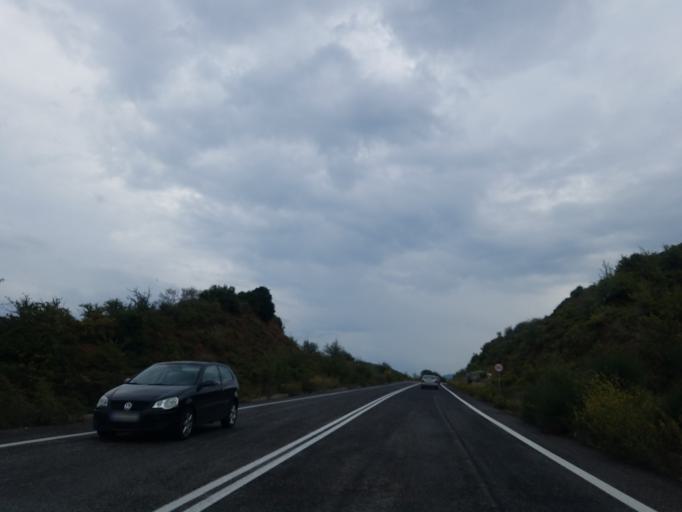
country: GR
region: Central Greece
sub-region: Nomos Voiotias
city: Livadeia
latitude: 38.4470
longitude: 22.7962
